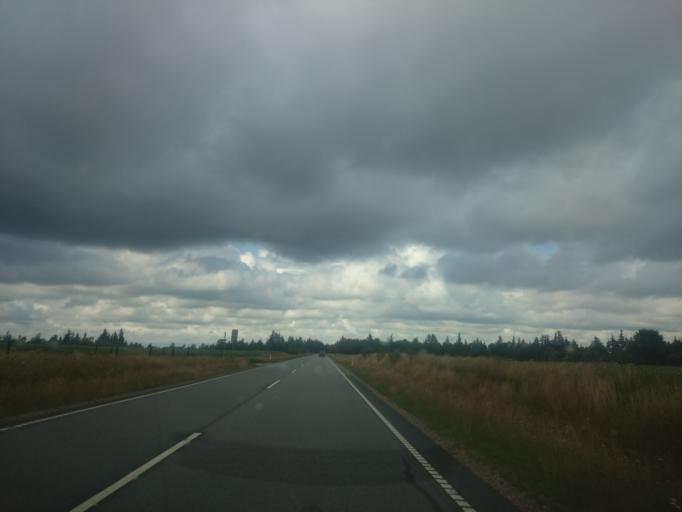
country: DK
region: South Denmark
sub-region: Billund Kommune
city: Grindsted
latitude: 55.6783
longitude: 8.9595
